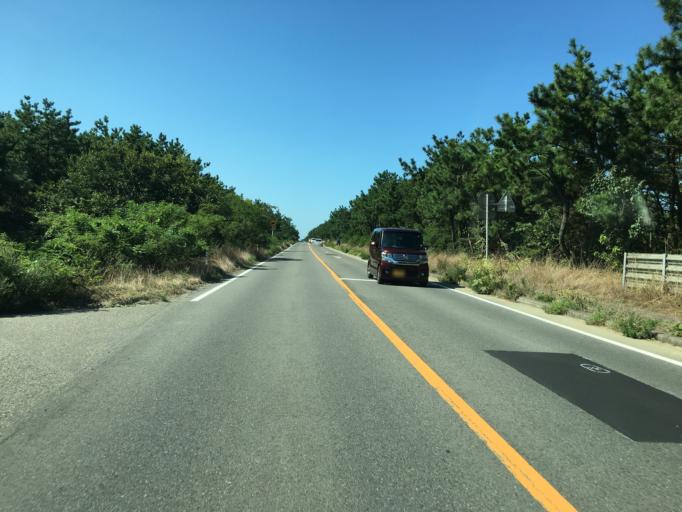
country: JP
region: Niigata
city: Niigata-shi
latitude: 37.9050
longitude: 138.9968
